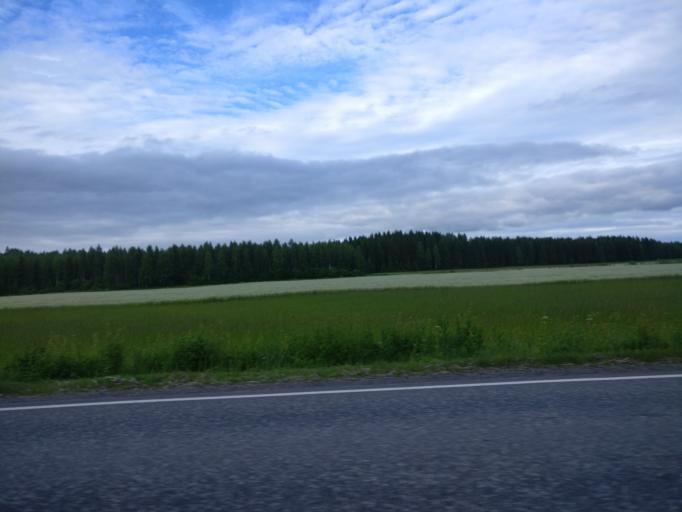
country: FI
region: Southern Savonia
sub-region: Savonlinna
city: Savonlinna
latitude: 61.8836
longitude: 28.9406
